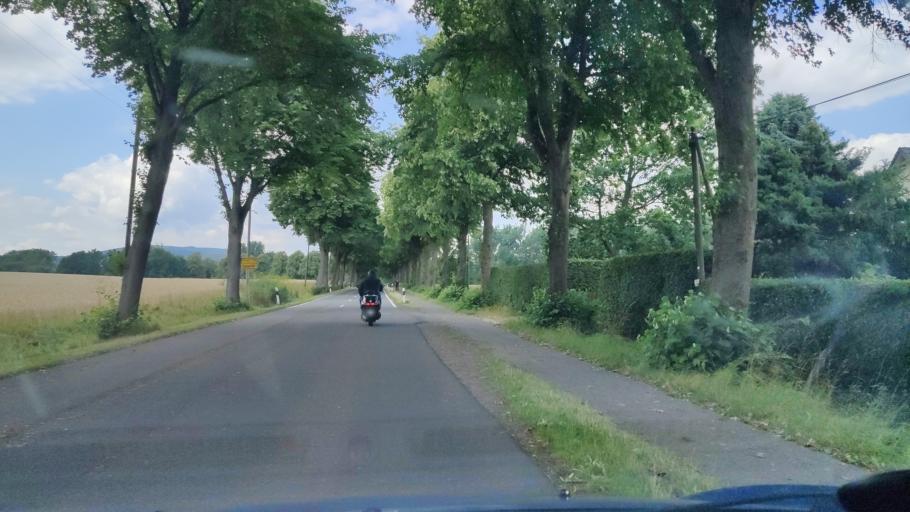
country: DE
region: Lower Saxony
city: Bad Munder am Deister
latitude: 52.1445
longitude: 9.4563
